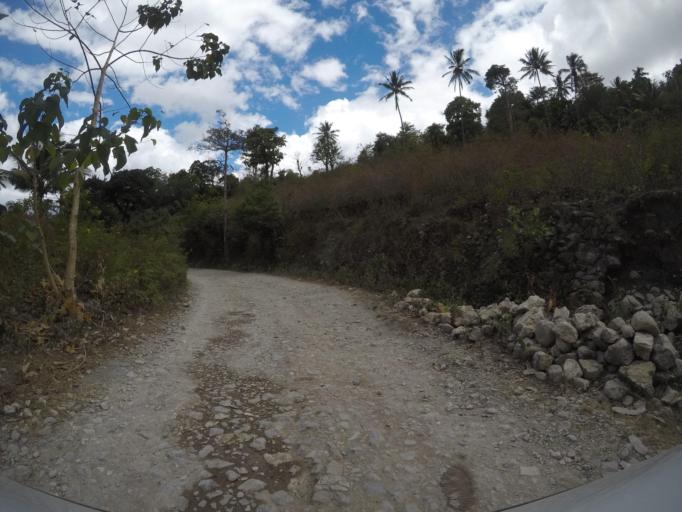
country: TL
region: Baucau
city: Baucau
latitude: -8.5254
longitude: 126.6894
